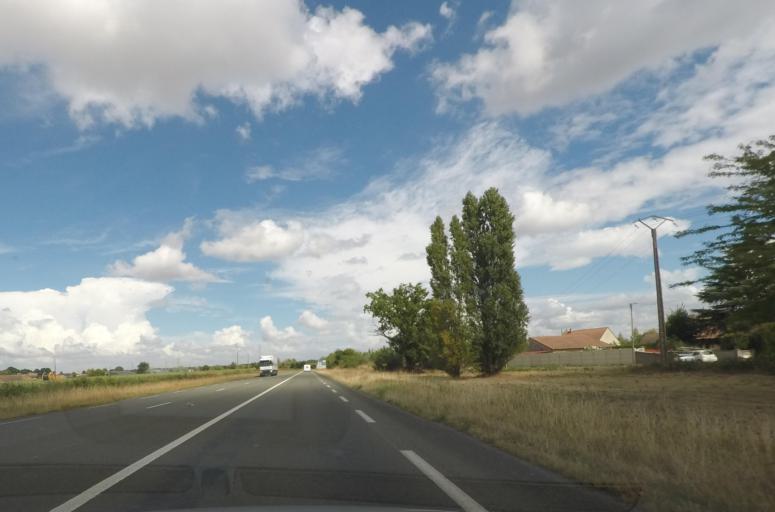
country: FR
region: Pays de la Loire
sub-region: Departement de la Sarthe
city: Spay
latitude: 47.9275
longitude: 0.1612
